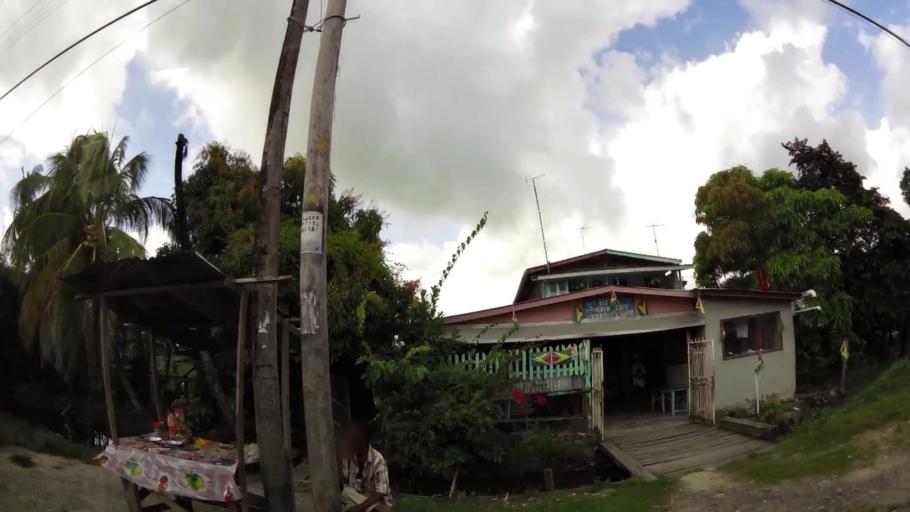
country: GY
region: Demerara-Mahaica
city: Mahaica Village
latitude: 6.6707
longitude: -57.9249
